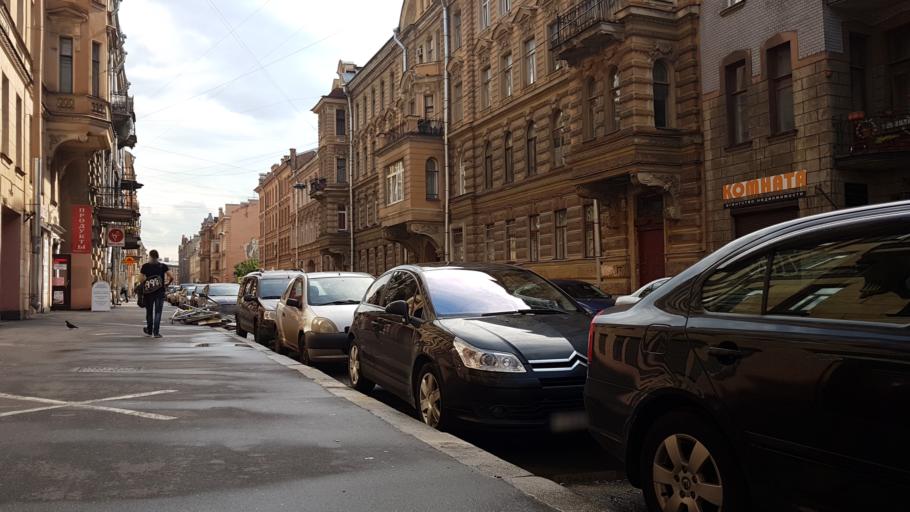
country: RU
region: St.-Petersburg
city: Centralniy
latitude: 59.9252
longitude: 30.3544
